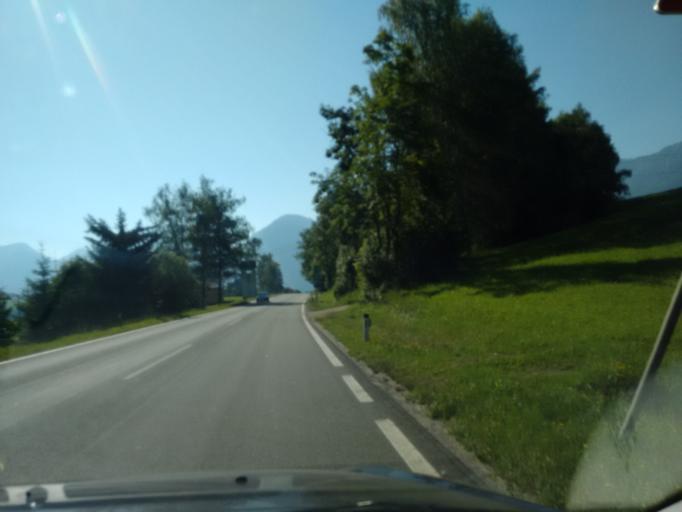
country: AT
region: Styria
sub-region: Politischer Bezirk Liezen
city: Altaussee
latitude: 47.6191
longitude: 13.7589
